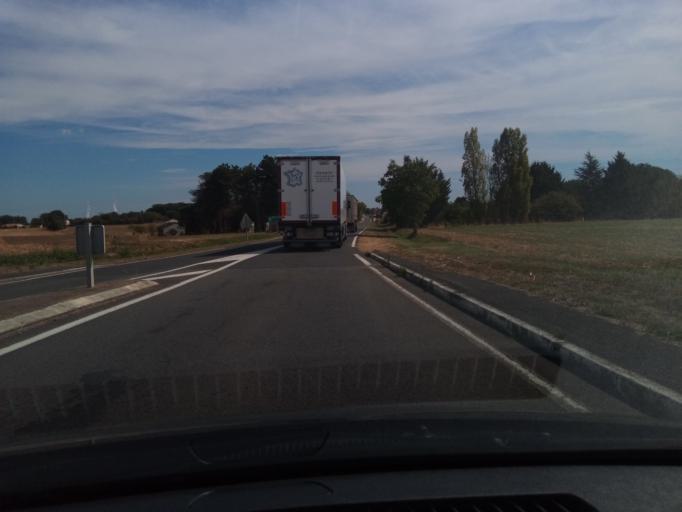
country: FR
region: Poitou-Charentes
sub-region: Departement de la Vienne
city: Terce
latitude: 46.4821
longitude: 0.5138
